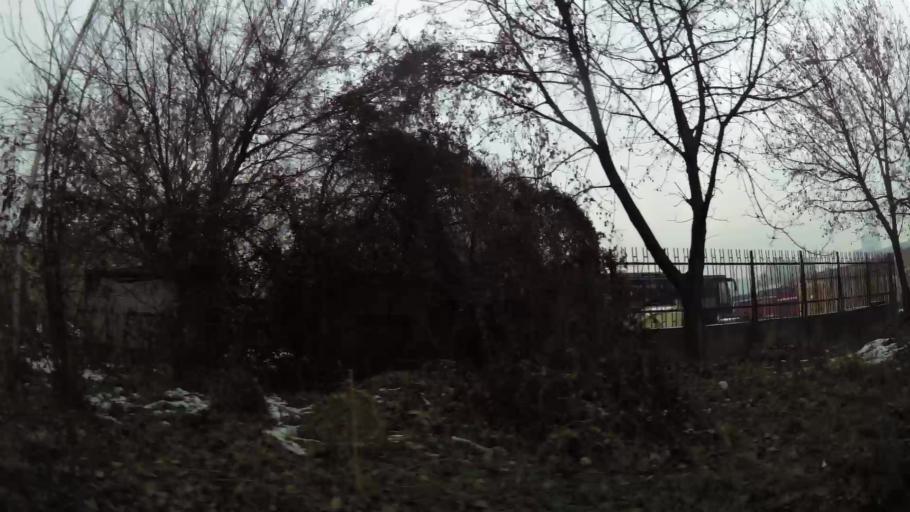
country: MK
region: Cair
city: Cair
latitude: 41.9993
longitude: 21.4630
